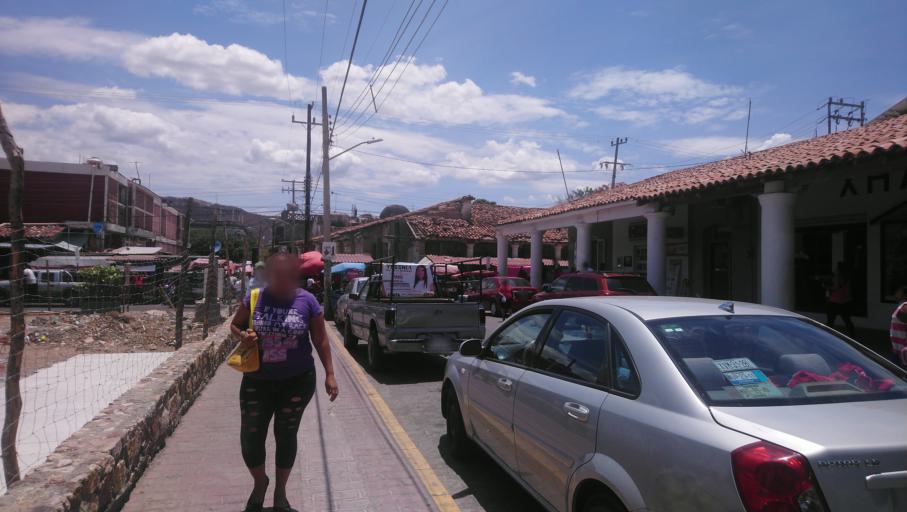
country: MX
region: Oaxaca
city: San Blas Atempa
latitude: 16.3329
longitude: -95.2320
